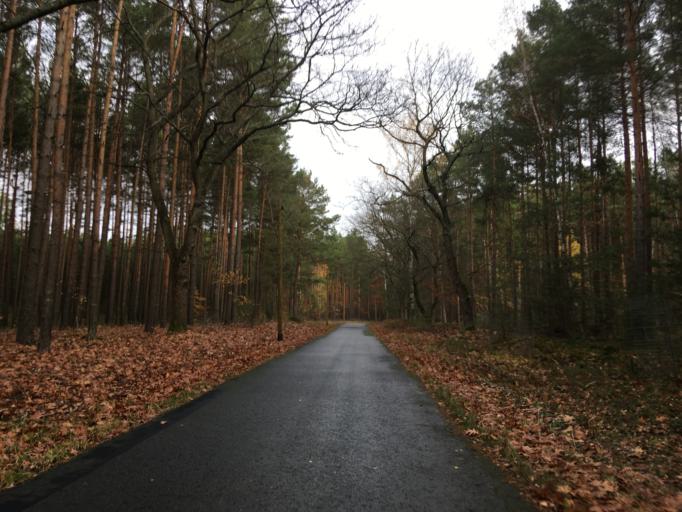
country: DE
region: Brandenburg
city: Tauer
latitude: 51.9144
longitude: 14.4656
